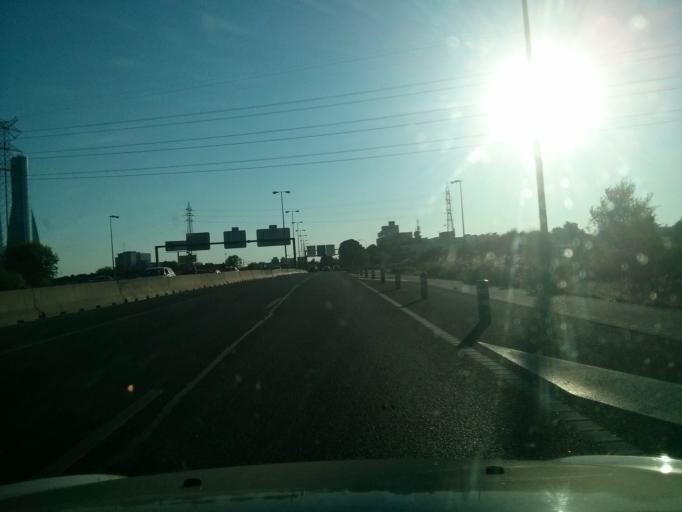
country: ES
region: Madrid
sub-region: Provincia de Madrid
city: Pinar de Chamartin
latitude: 40.4841
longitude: -3.6745
